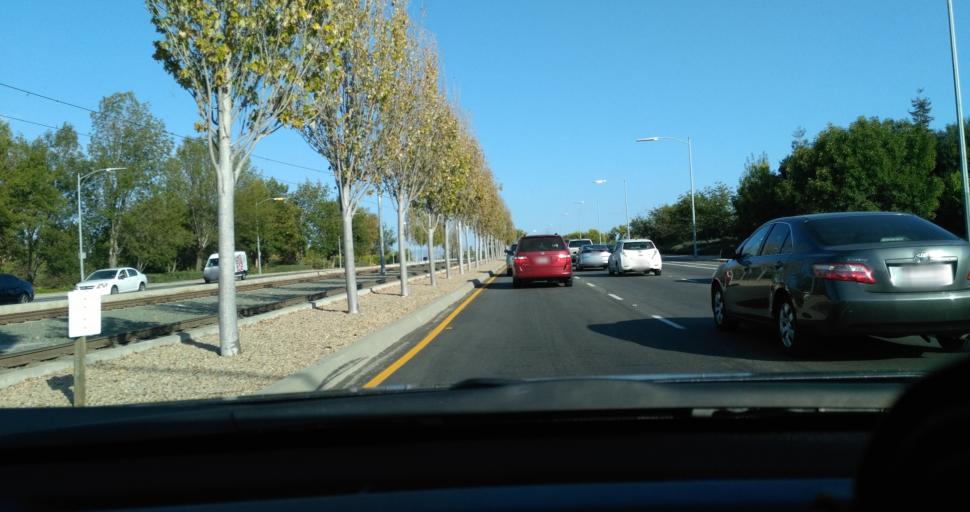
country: US
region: California
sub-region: Santa Clara County
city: Milpitas
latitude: 37.4121
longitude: -121.9278
